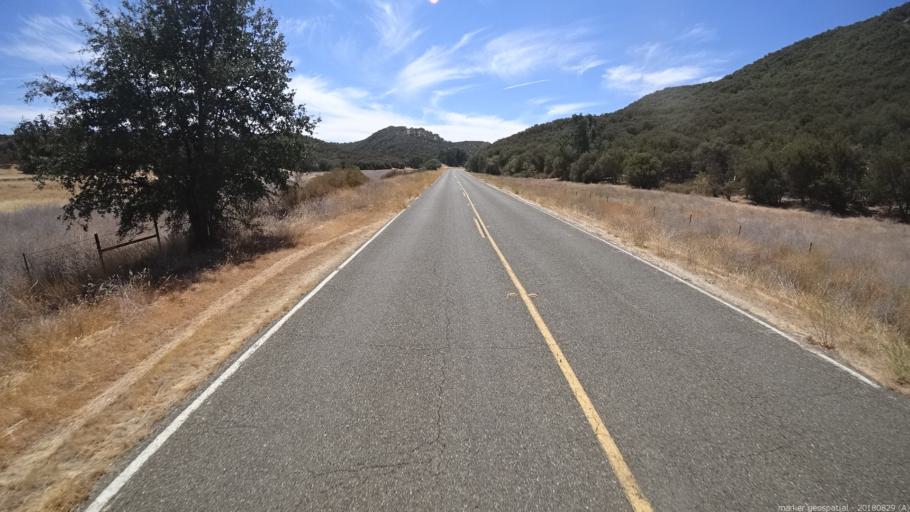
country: US
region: California
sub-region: San Luis Obispo County
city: Lake Nacimiento
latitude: 35.8733
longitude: -121.0640
